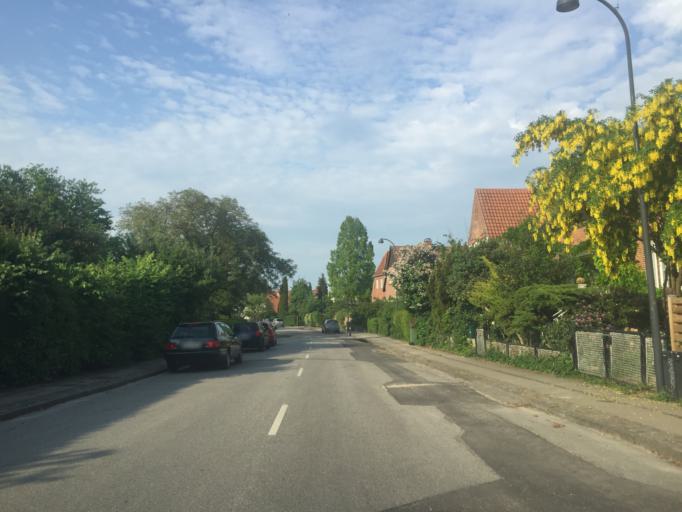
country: DK
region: Capital Region
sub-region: Gentofte Kommune
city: Charlottenlund
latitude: 55.7442
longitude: 12.5620
